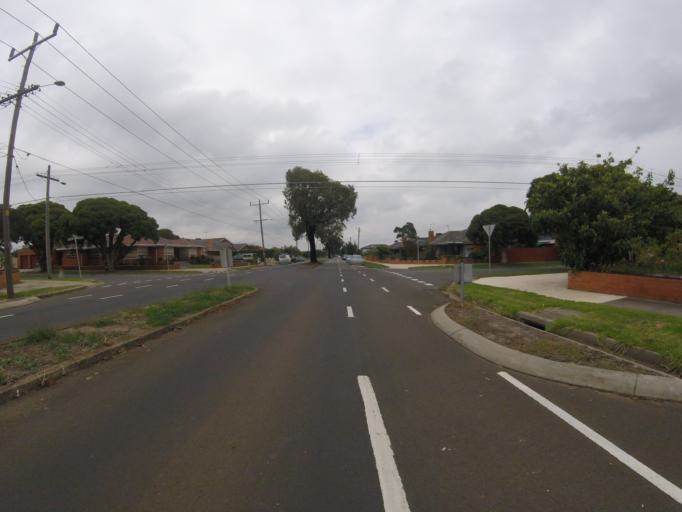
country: AU
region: Victoria
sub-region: Darebin
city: Reservoir
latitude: -37.7018
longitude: 145.0025
